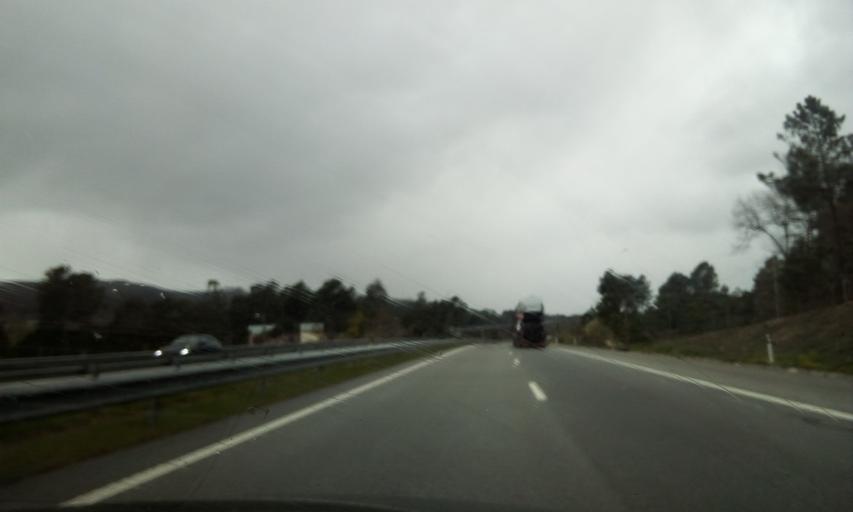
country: PT
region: Guarda
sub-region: Fornos de Algodres
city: Fornos de Algodres
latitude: 40.6134
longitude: -7.6419
